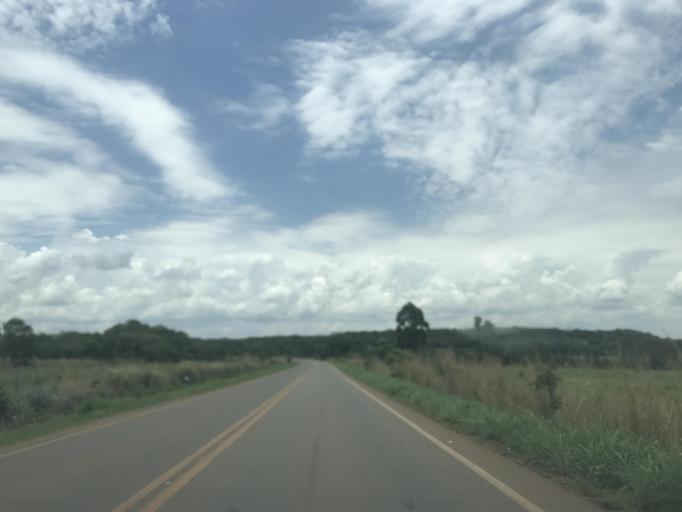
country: BR
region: Goias
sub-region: Vianopolis
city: Vianopolis
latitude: -16.7247
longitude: -48.4255
